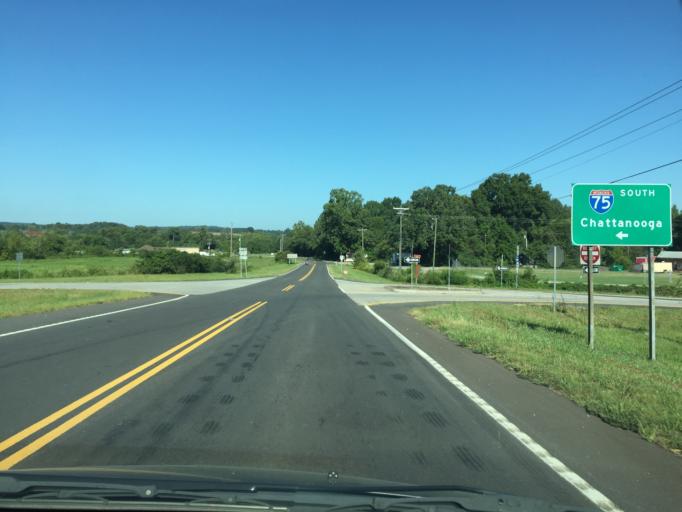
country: US
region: Tennessee
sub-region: Monroe County
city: Sweetwater
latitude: 35.6235
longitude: -84.4927
